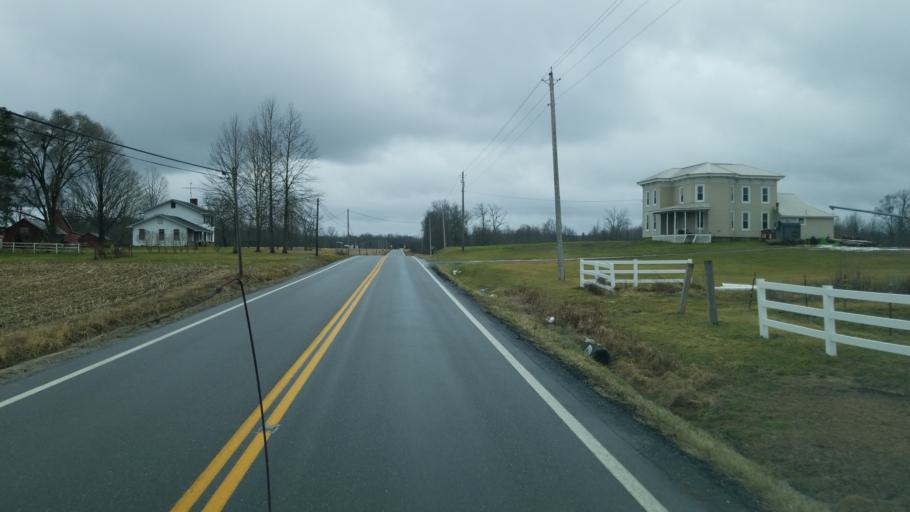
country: US
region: Ohio
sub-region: Trumbull County
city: Champion Heights
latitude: 41.3469
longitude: -80.9545
